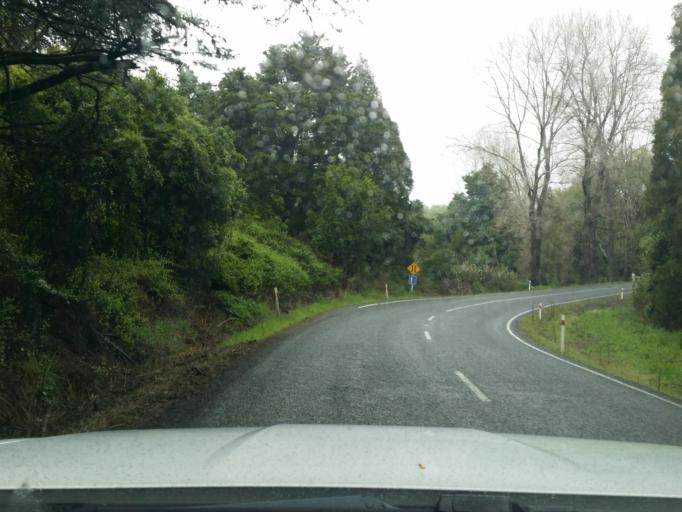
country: NZ
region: Northland
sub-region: Kaipara District
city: Dargaville
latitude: -35.7488
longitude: 173.9051
